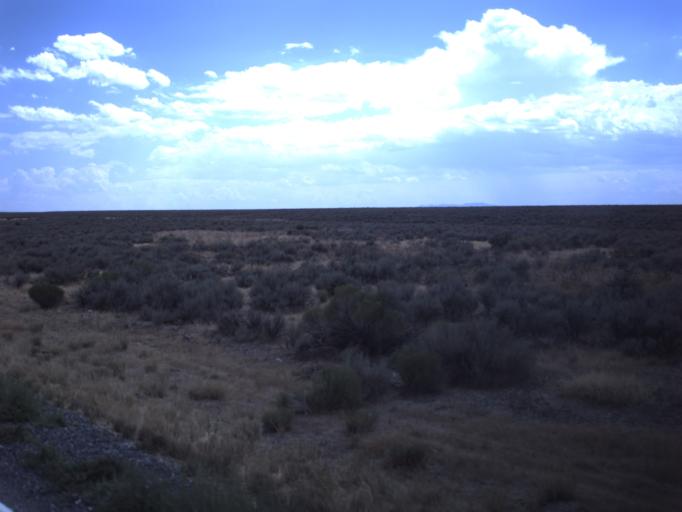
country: US
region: Utah
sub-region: Tooele County
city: Tooele
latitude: 40.3781
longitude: -112.3788
